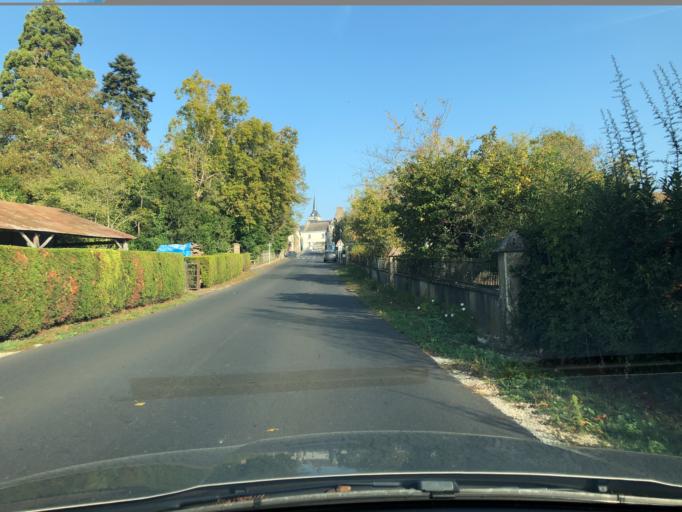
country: FR
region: Centre
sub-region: Departement d'Indre-et-Loire
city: Neuvy-le-Roi
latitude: 47.6561
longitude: 0.6489
